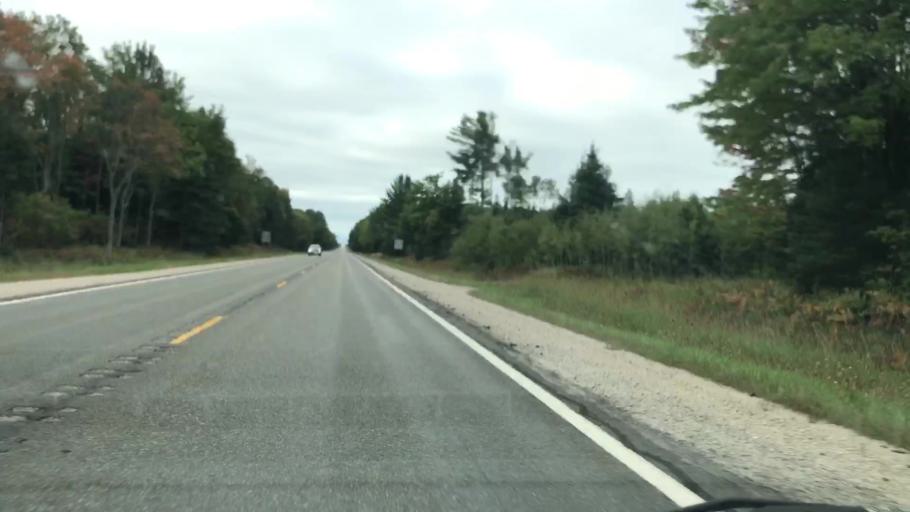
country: US
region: Michigan
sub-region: Luce County
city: Newberry
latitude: 46.2322
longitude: -85.5722
